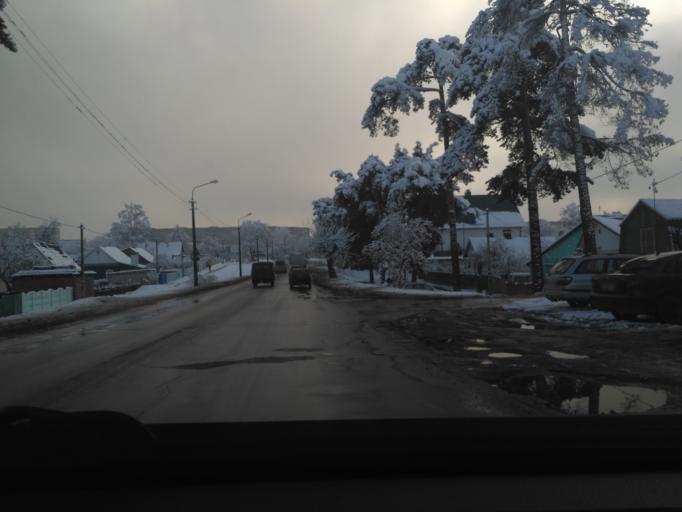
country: BY
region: Minsk
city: Horad Barysaw
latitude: 54.2281
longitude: 28.4936
